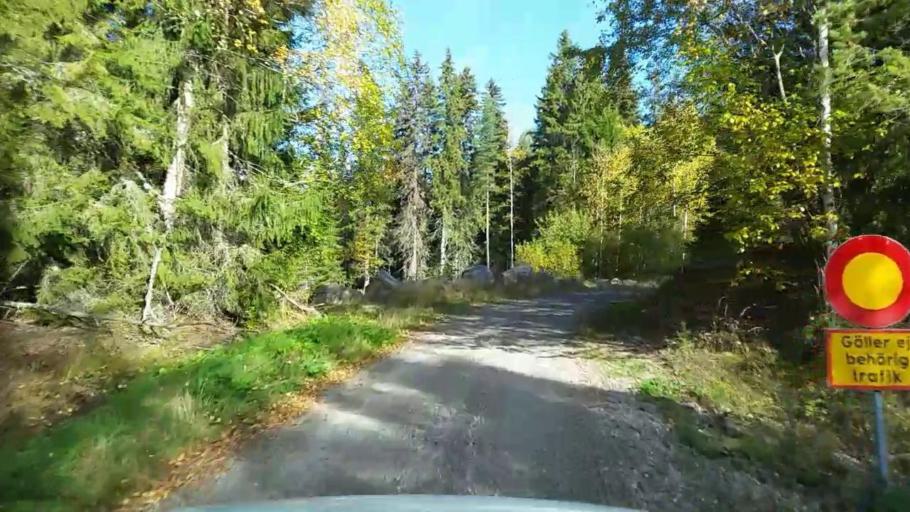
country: SE
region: Gaevleborg
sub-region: Ljusdals Kommun
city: Jaervsoe
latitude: 61.7871
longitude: 16.1516
